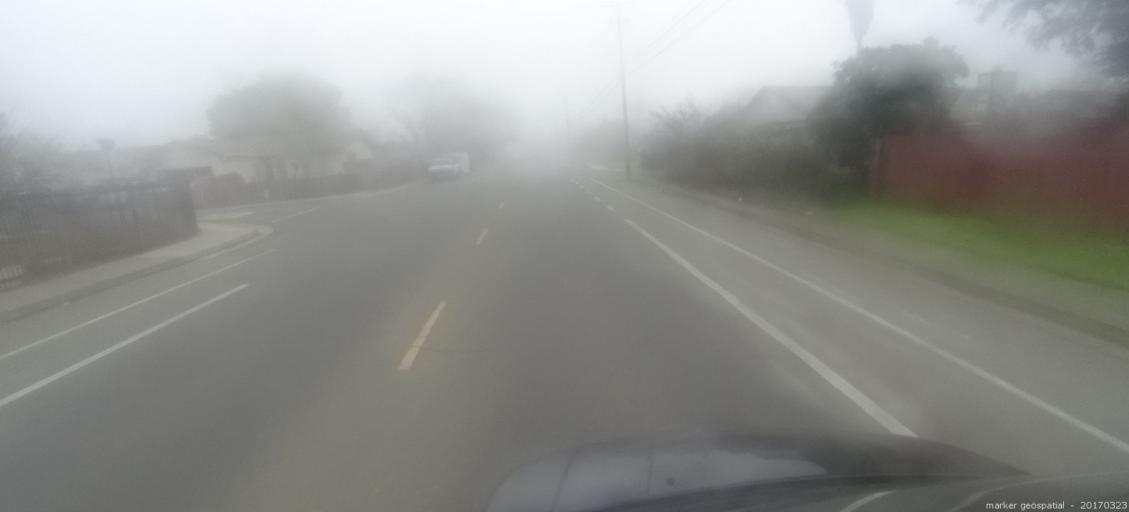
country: US
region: California
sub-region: Sacramento County
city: Florin
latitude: 38.5160
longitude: -121.4242
